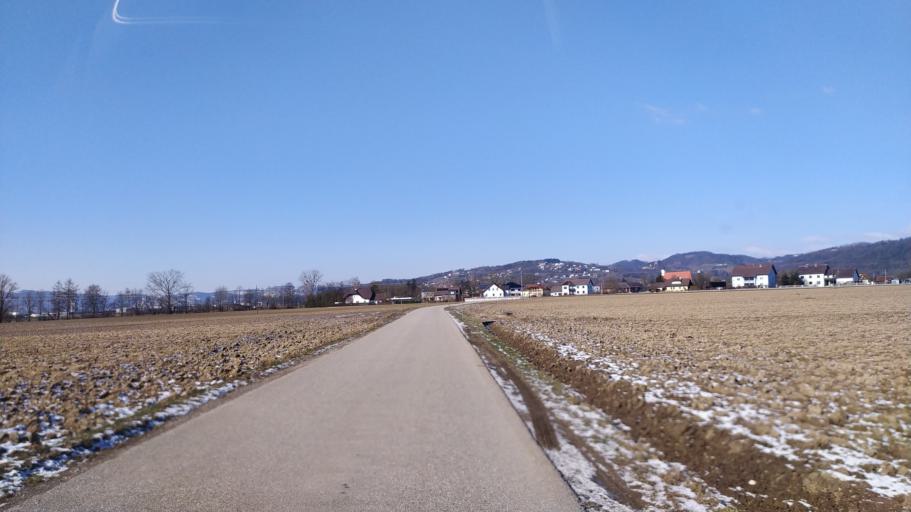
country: AT
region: Upper Austria
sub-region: Politischer Bezirk Urfahr-Umgebung
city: Feldkirchen an der Donau
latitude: 48.3438
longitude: 14.0769
